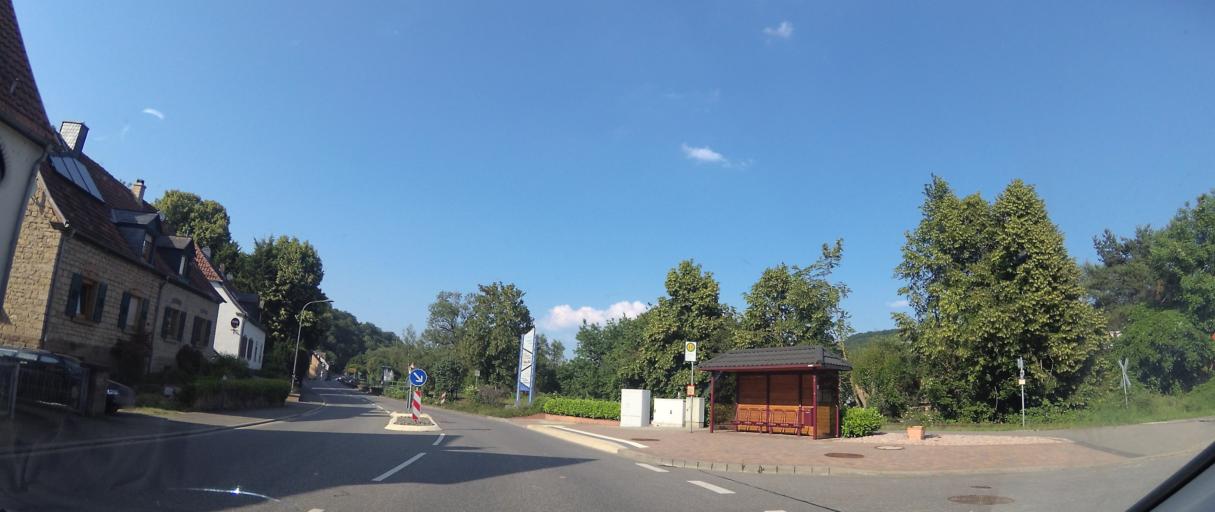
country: DE
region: Rheinland-Pfalz
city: Odenbach
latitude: 49.6846
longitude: 7.6482
